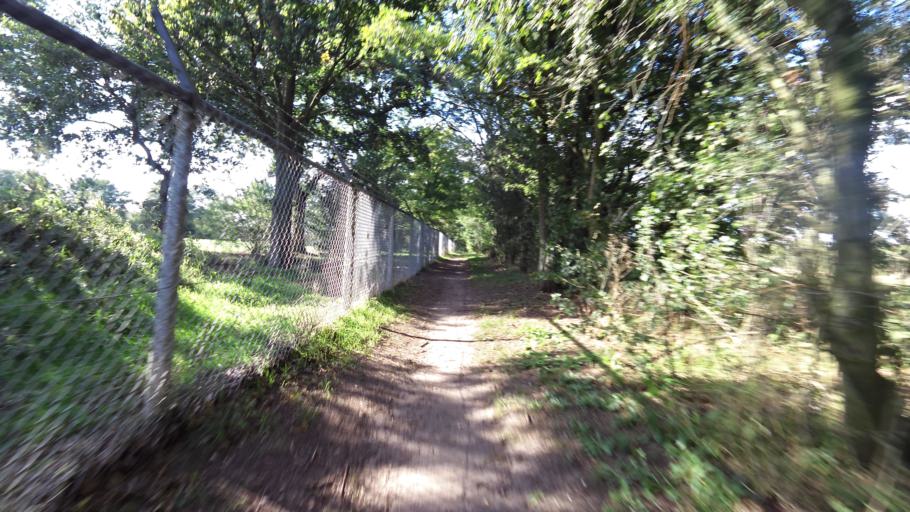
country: NL
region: Gelderland
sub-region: Gemeente Renkum
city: Heelsum
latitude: 51.9904
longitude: 5.7610
